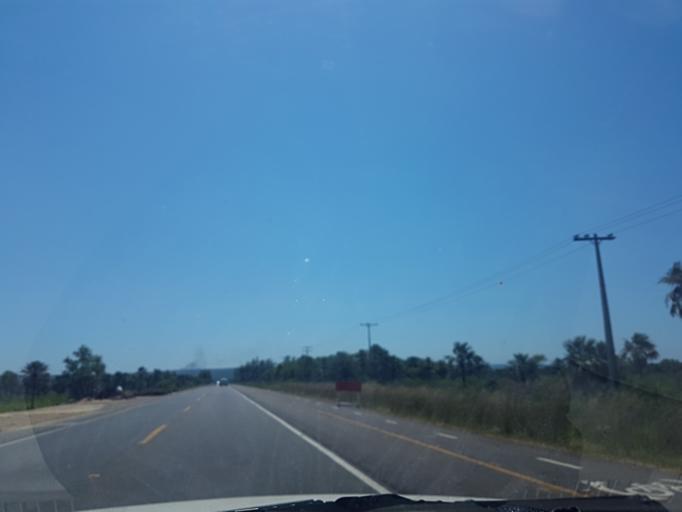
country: PY
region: Cordillera
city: Emboscada
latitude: -25.2088
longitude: -57.3935
